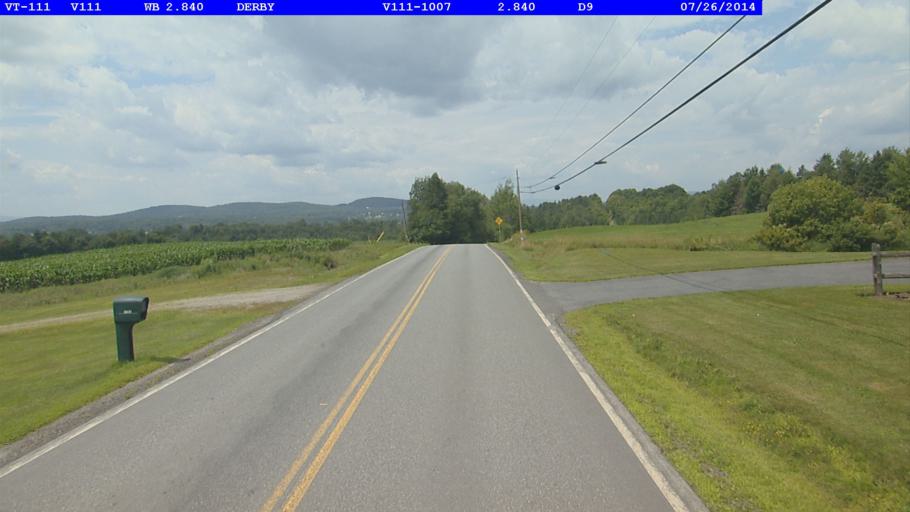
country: US
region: Vermont
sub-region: Orleans County
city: Newport
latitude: 44.9367
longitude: -72.0833
